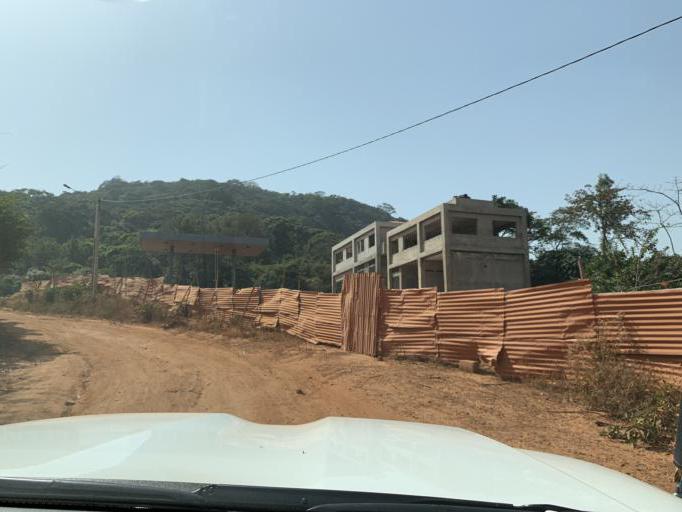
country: GN
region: Mamou
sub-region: Dalaba
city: Dalaba
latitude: 10.7262
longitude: -12.2527
